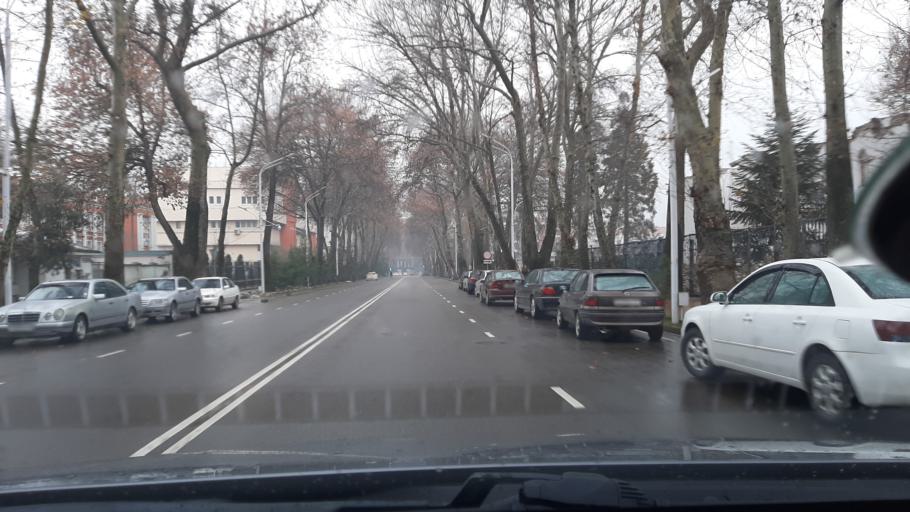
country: TJ
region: Dushanbe
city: Dushanbe
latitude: 38.5729
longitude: 68.7857
